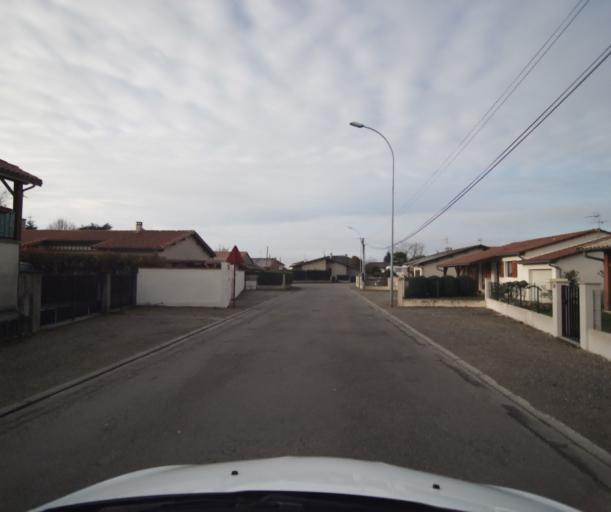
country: FR
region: Midi-Pyrenees
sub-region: Departement du Tarn-et-Garonne
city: Castelsarrasin
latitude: 44.0430
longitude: 1.1006
